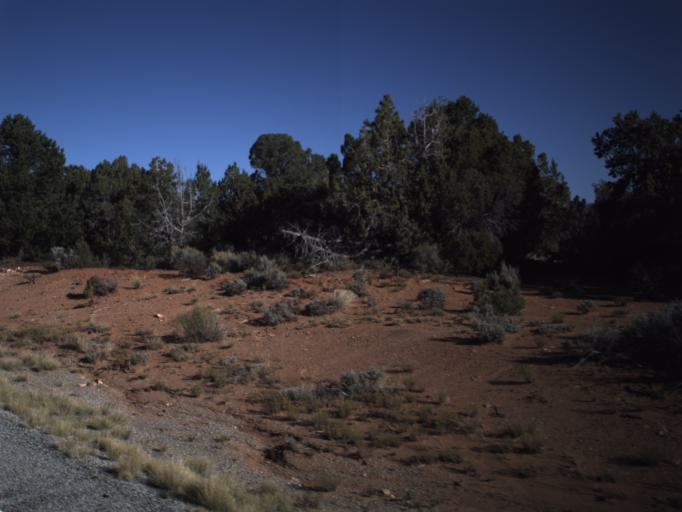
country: US
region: Utah
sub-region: San Juan County
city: Blanding
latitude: 37.5463
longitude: -109.9849
